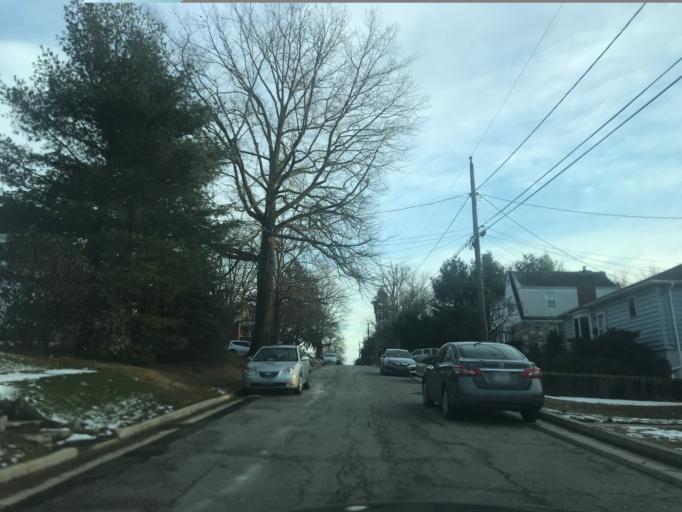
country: US
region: Maryland
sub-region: Baltimore County
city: Catonsville
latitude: 39.2784
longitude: -76.7286
